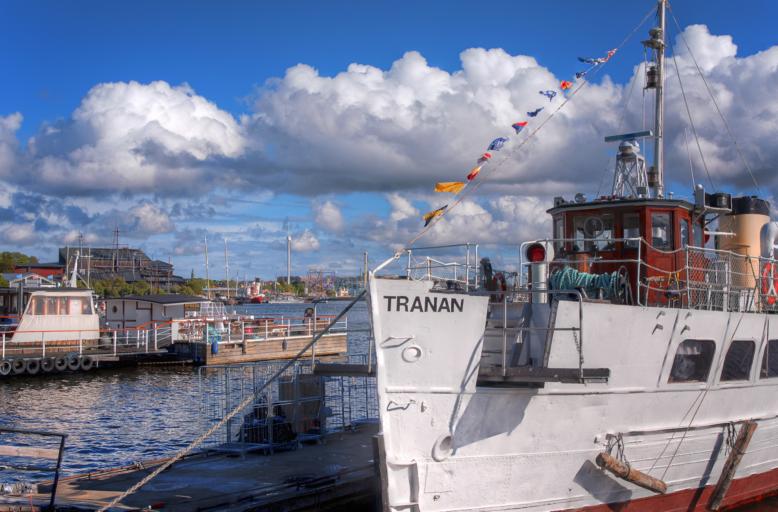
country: SE
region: Stockholm
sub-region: Stockholms Kommun
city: OEstermalm
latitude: 59.3383
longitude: 18.0804
